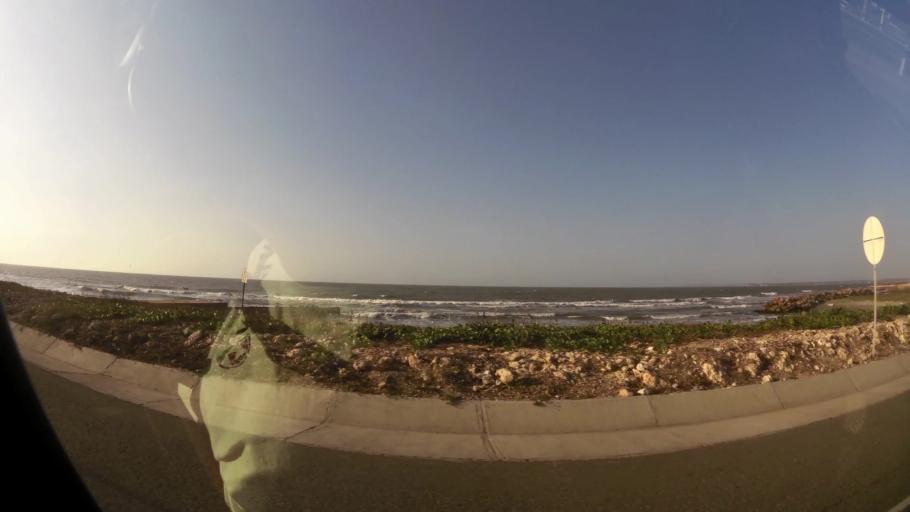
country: CO
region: Bolivar
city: Cartagena
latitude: 10.4517
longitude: -75.5162
